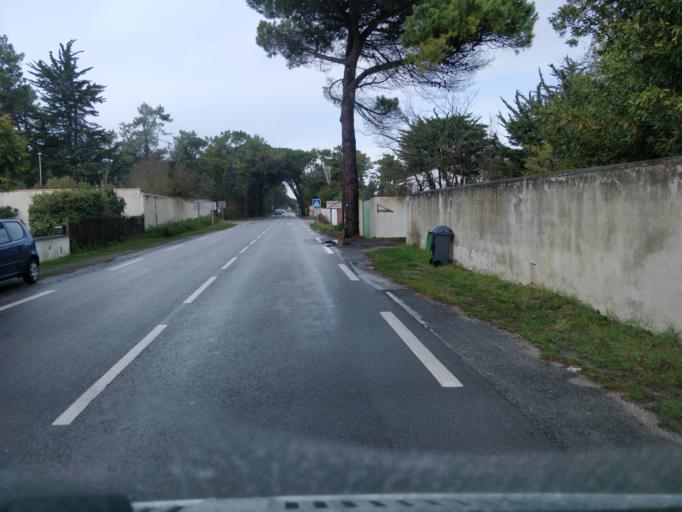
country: FR
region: Poitou-Charentes
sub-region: Departement de la Charente-Maritime
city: Rivedoux-Plage
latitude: 46.1722
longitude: -1.2848
